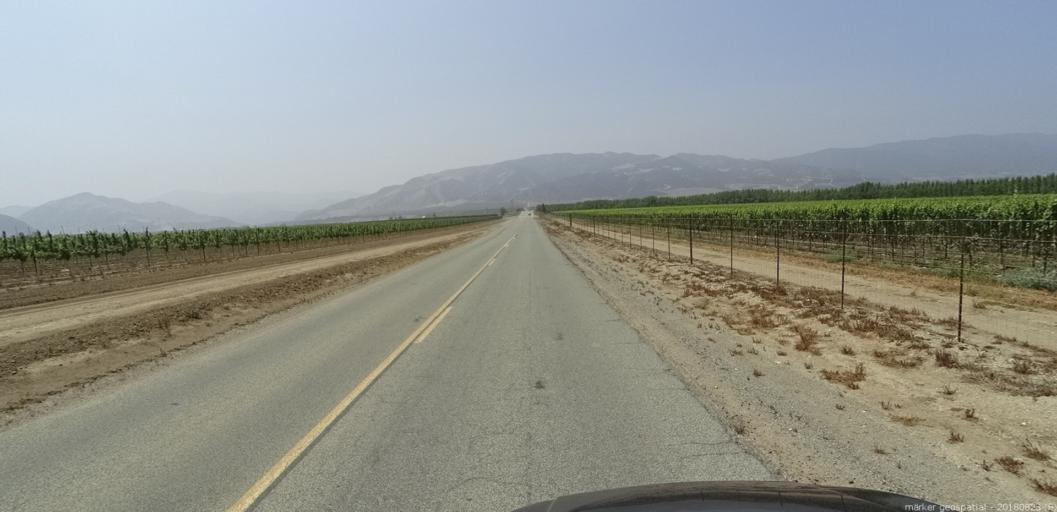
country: US
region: California
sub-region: Monterey County
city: Greenfield
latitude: 36.3257
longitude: -121.2867
